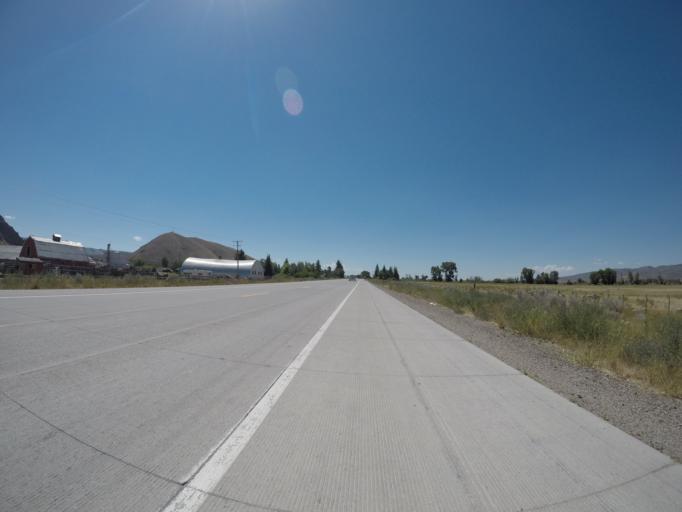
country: US
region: Idaho
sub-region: Bear Lake County
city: Montpelier
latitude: 42.0993
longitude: -110.9527
